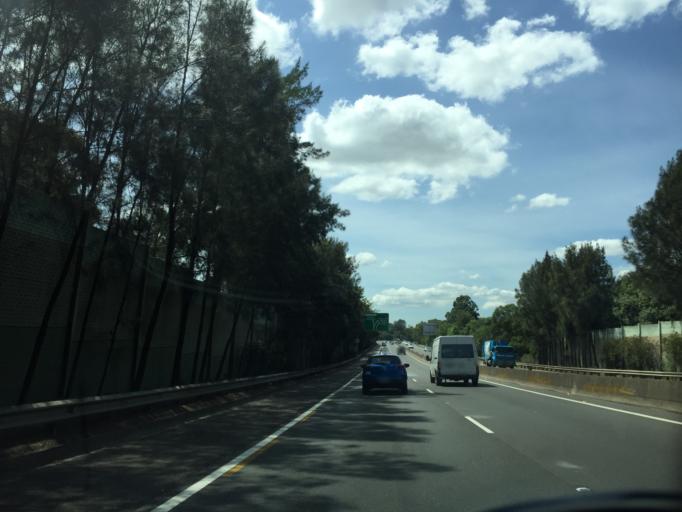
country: AU
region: New South Wales
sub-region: Parramatta
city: Telopea
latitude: -33.7989
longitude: 151.0172
